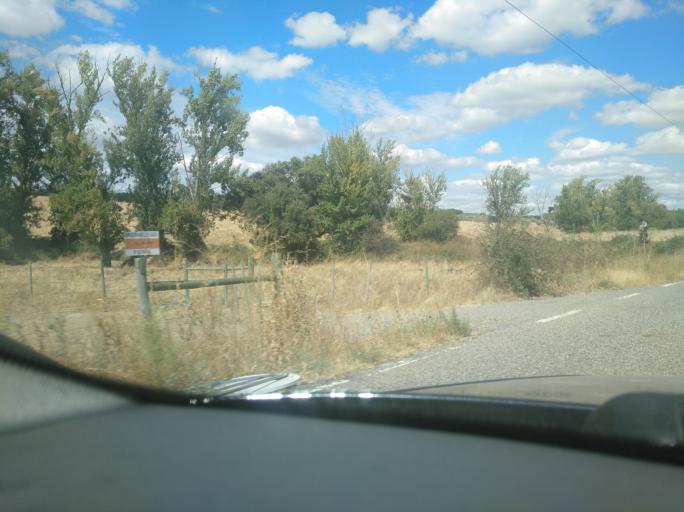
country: PT
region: Portalegre
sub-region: Arronches
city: Arronches
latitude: 39.0827
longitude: -7.3598
